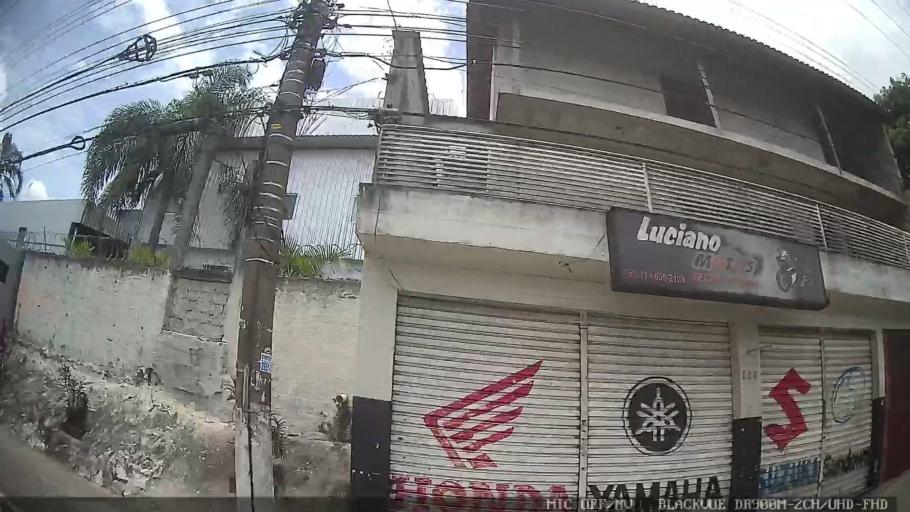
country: BR
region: Sao Paulo
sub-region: Poa
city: Poa
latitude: -23.5324
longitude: -46.3488
